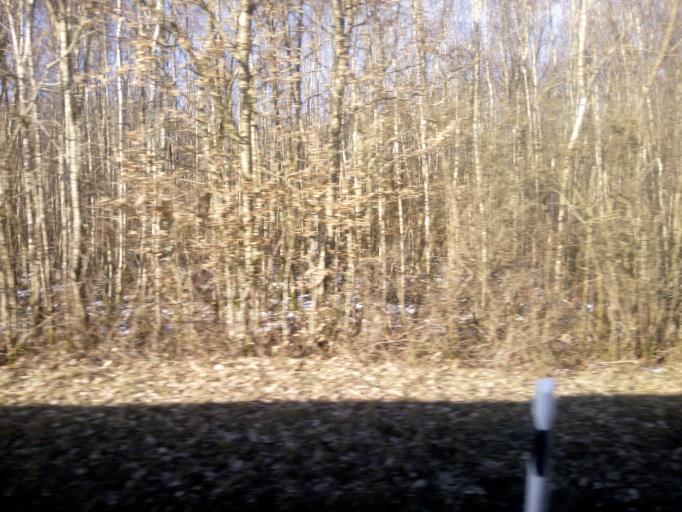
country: LU
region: Grevenmacher
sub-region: Canton d'Echternach
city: Consdorf
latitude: 49.7919
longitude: 6.3457
